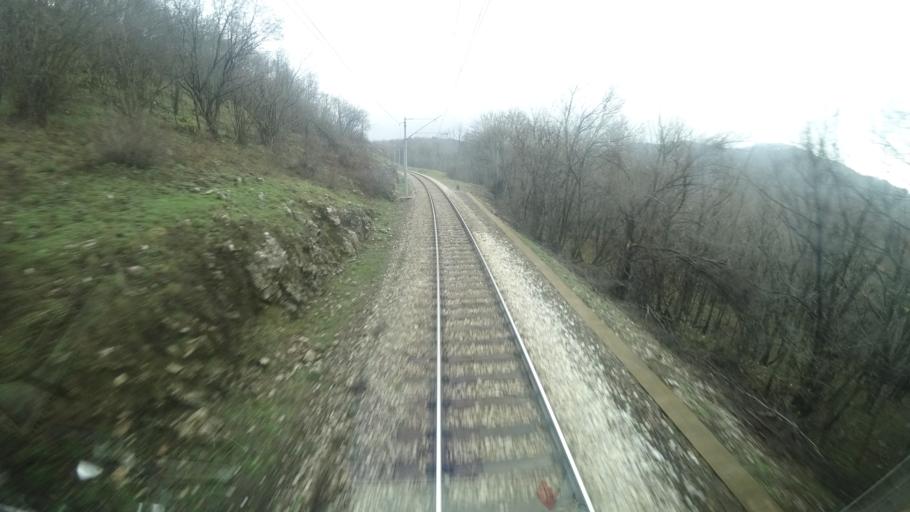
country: HR
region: Primorsko-Goranska
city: Hreljin
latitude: 45.2927
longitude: 14.6439
